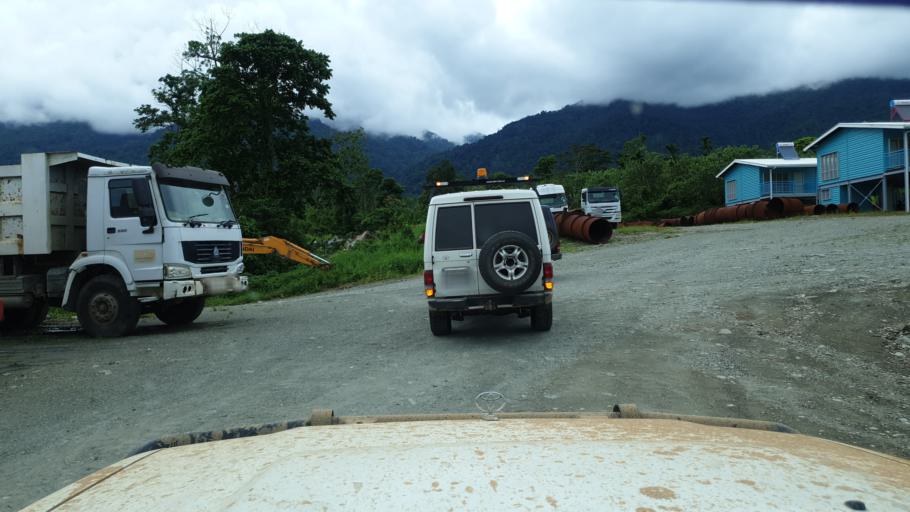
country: PG
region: Northern Province
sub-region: Sohe
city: Kokoda
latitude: -8.9417
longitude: 147.8679
